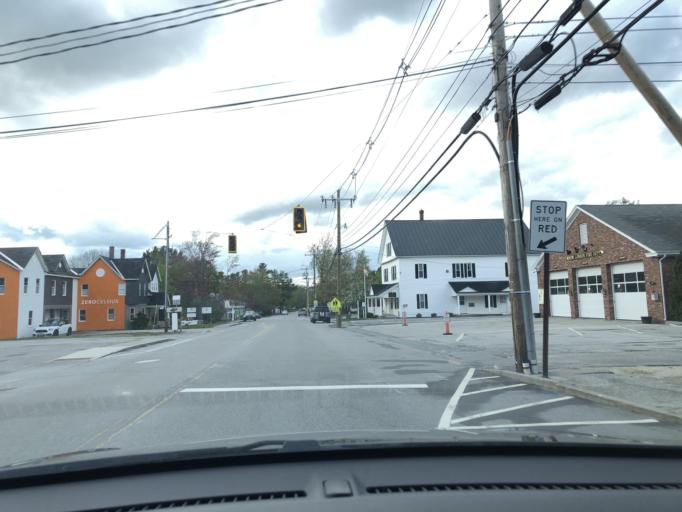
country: US
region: New Hampshire
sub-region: Merrimack County
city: New London
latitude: 43.4152
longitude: -71.9865
